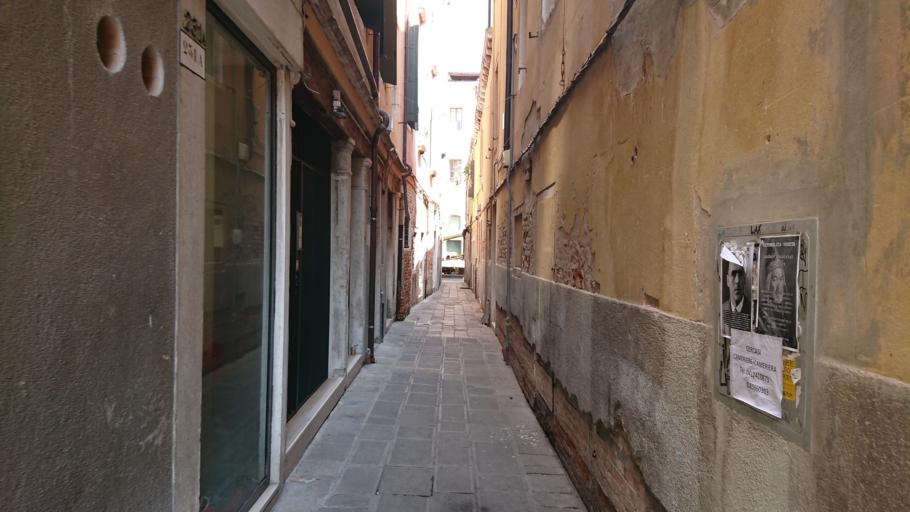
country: IT
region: Veneto
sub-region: Provincia di Venezia
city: Venice
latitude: 45.4391
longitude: 12.3345
